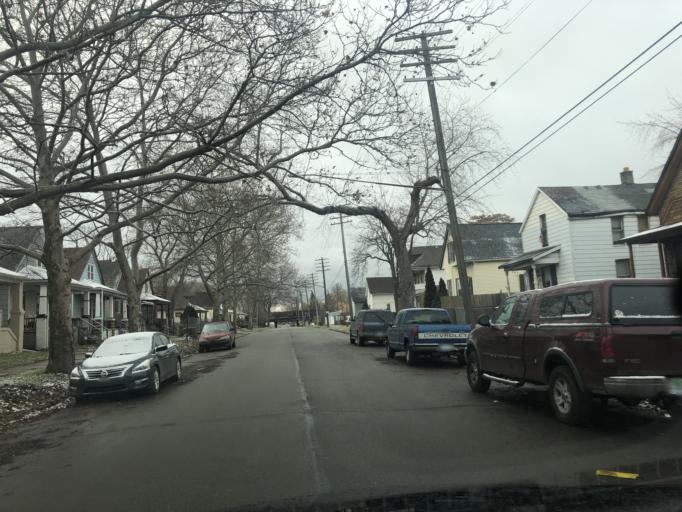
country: US
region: Michigan
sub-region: Wayne County
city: River Rouge
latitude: 42.3263
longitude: -83.1153
